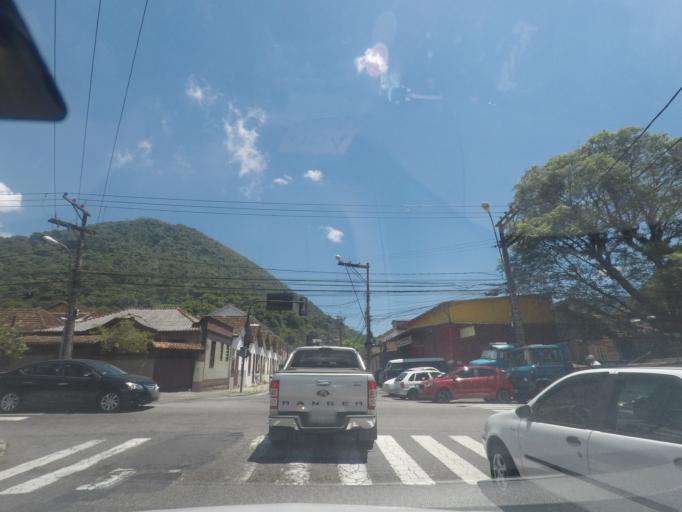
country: BR
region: Rio de Janeiro
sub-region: Petropolis
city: Petropolis
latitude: -22.5280
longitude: -43.1728
